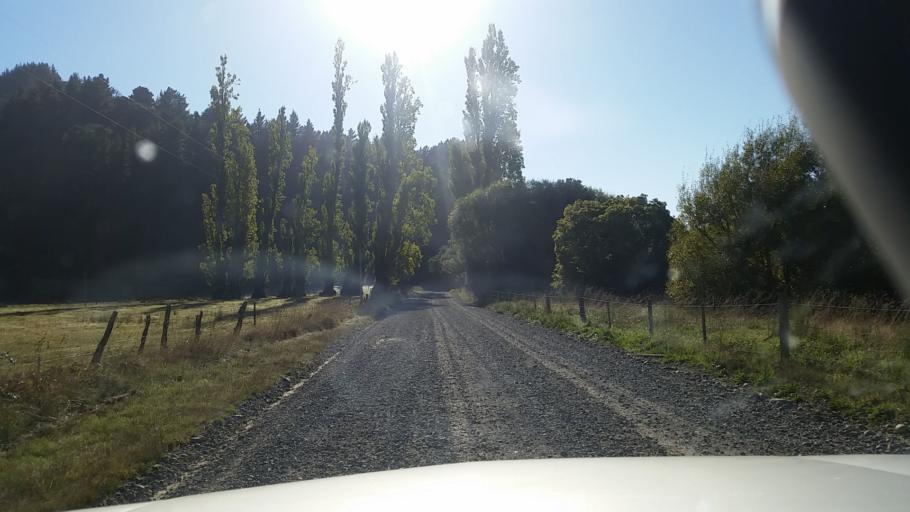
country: NZ
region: Marlborough
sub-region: Marlborough District
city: Blenheim
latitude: -41.4480
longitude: 173.8777
